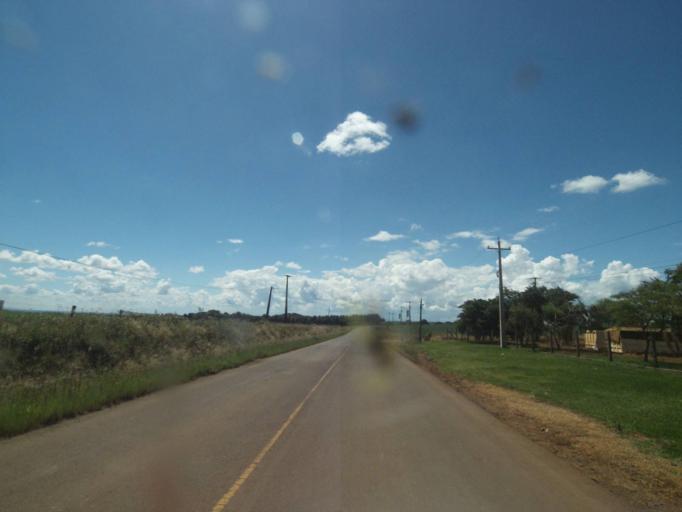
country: BR
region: Parana
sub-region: Pinhao
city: Pinhao
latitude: -25.8264
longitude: -52.0382
